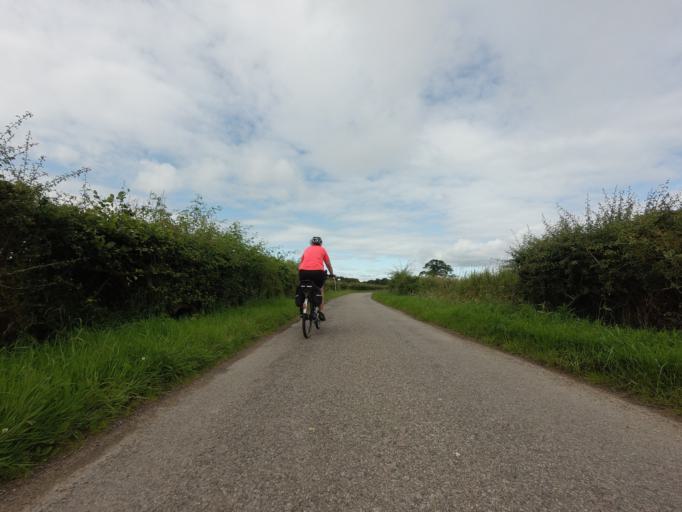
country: GB
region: Scotland
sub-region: Moray
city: Hopeman
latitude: 57.6700
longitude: -3.3884
